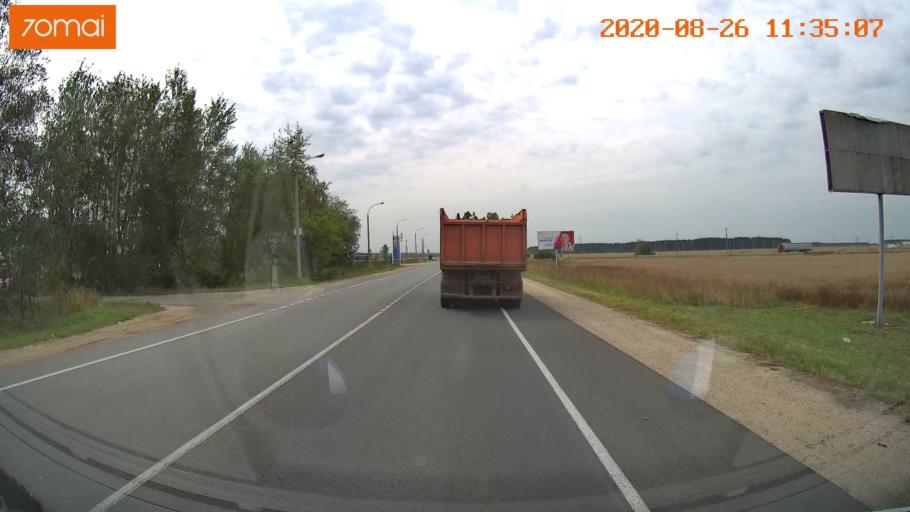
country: RU
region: Rjazan
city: Shilovo
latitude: 54.2780
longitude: 40.8372
